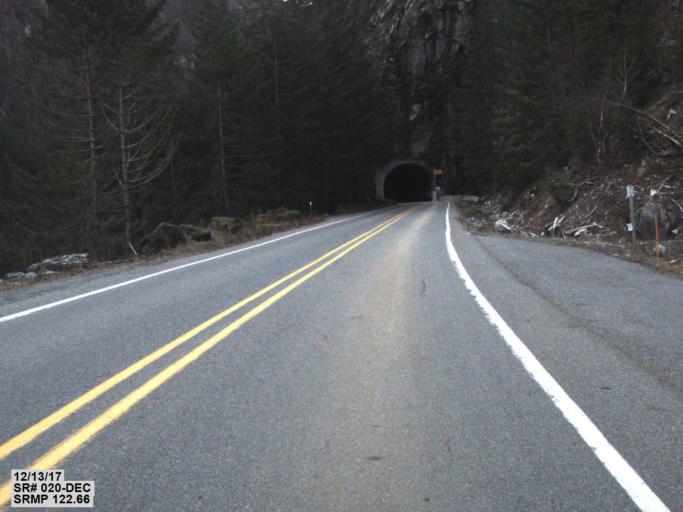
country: US
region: Washington
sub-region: Snohomish County
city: Darrington
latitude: 48.6933
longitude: -121.2216
